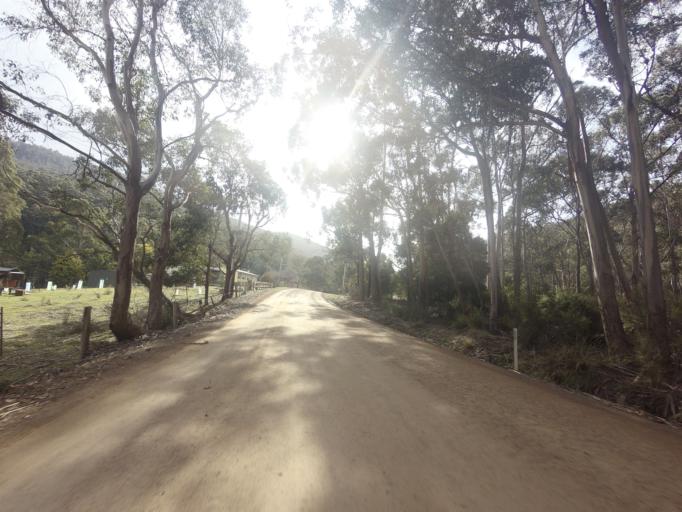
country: AU
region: Tasmania
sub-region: Huon Valley
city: Huonville
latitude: -43.0688
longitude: 147.0881
